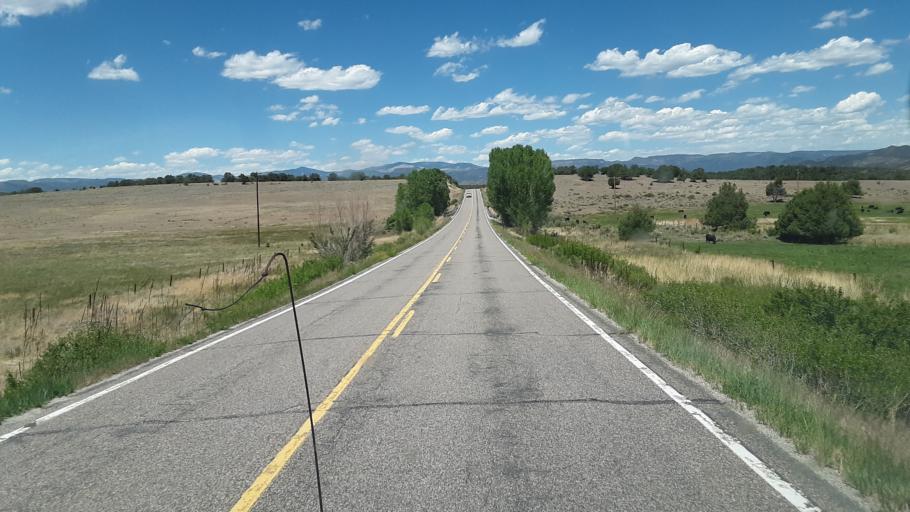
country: US
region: Colorado
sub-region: Custer County
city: Westcliffe
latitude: 38.2962
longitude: -105.6209
